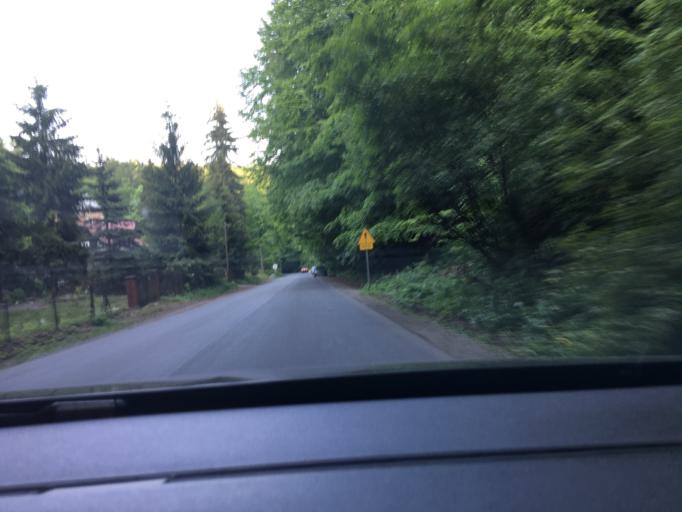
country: PL
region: Lesser Poland Voivodeship
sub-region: Powiat krakowski
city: Skala
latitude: 50.2113
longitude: 19.8260
